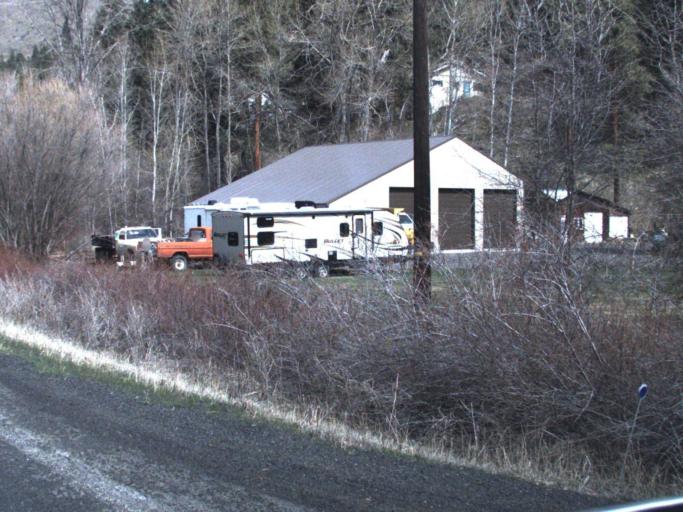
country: US
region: Washington
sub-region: Yakima County
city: Tieton
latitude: 46.8788
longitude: -120.9802
